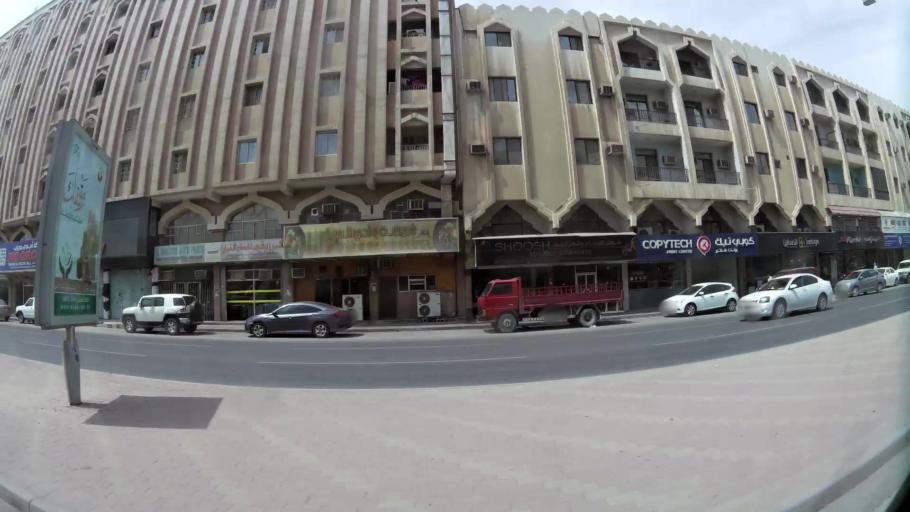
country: QA
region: Baladiyat ad Dawhah
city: Doha
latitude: 25.2776
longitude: 51.5407
